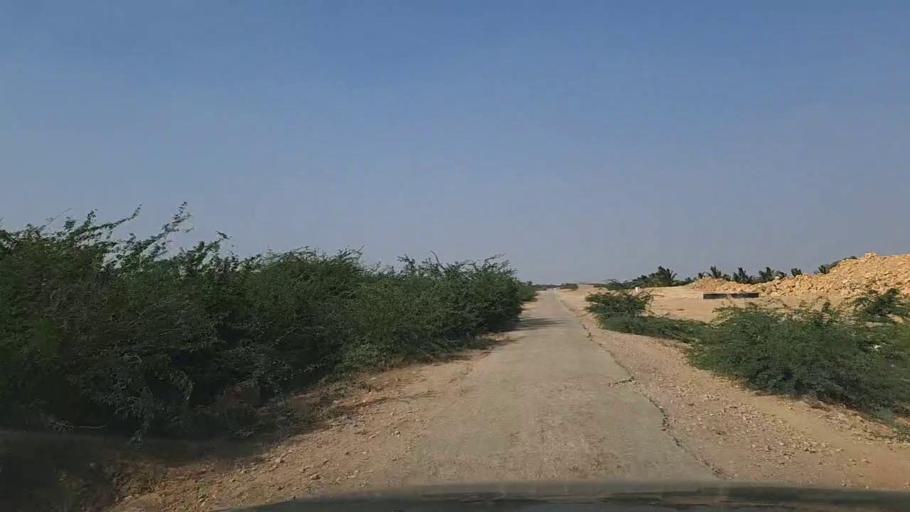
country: PK
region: Sindh
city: Gharo
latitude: 24.7571
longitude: 67.5797
